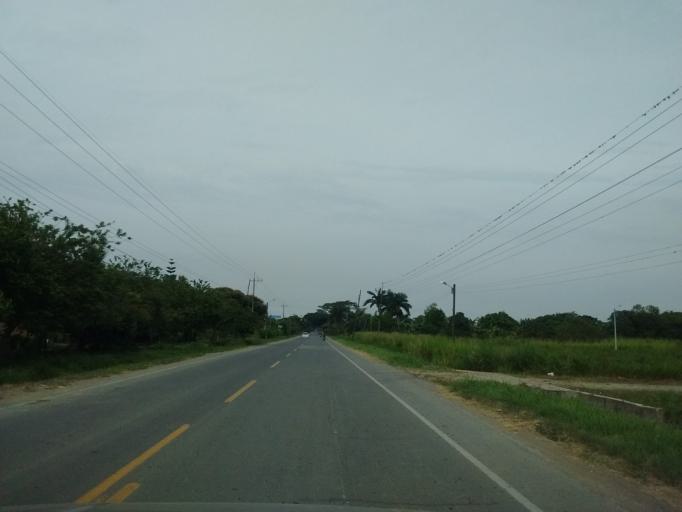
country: CO
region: Cauca
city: Puerto Tejada
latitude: 3.1839
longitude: -76.4510
